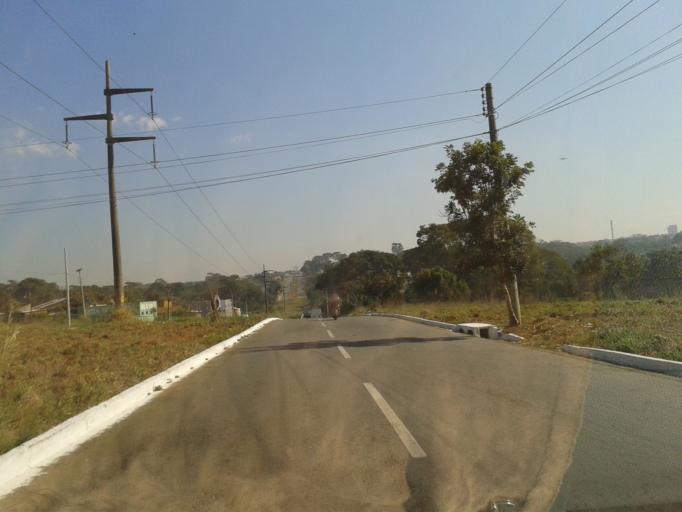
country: BR
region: Goias
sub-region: Aparecida De Goiania
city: Aparecida de Goiania
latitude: -16.7695
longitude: -49.2993
